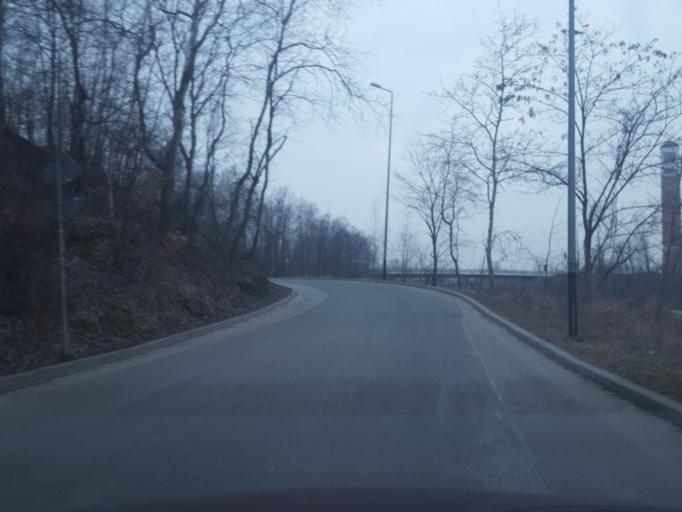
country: PL
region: Lesser Poland Voivodeship
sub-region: Krakow
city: Krakow
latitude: 50.0127
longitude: 19.9414
